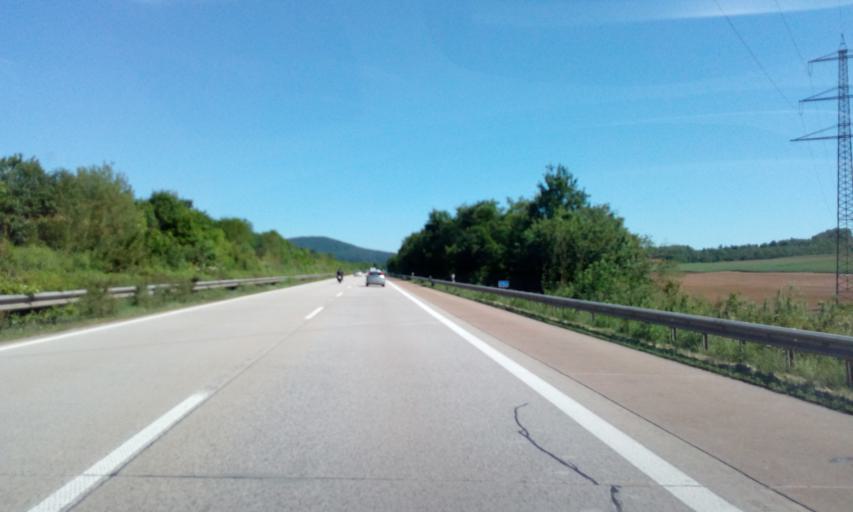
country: DE
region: Rheinland-Pfalz
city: Esch
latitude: 49.9114
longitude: 6.8549
